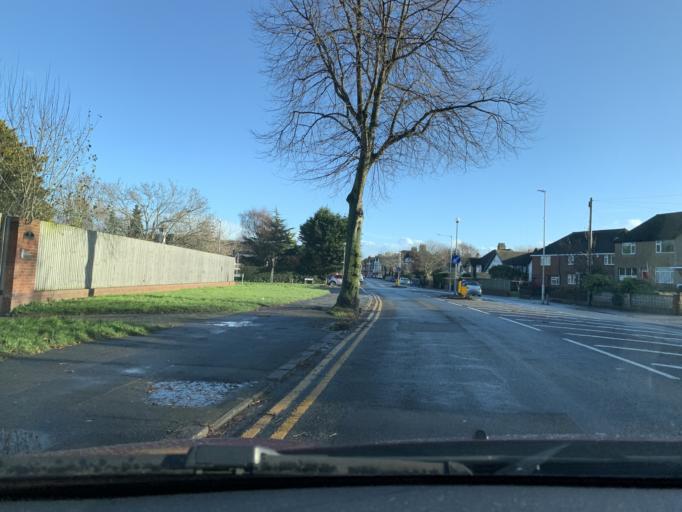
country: GB
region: England
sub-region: Kent
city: Folkestone
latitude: 51.0842
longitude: 1.1635
